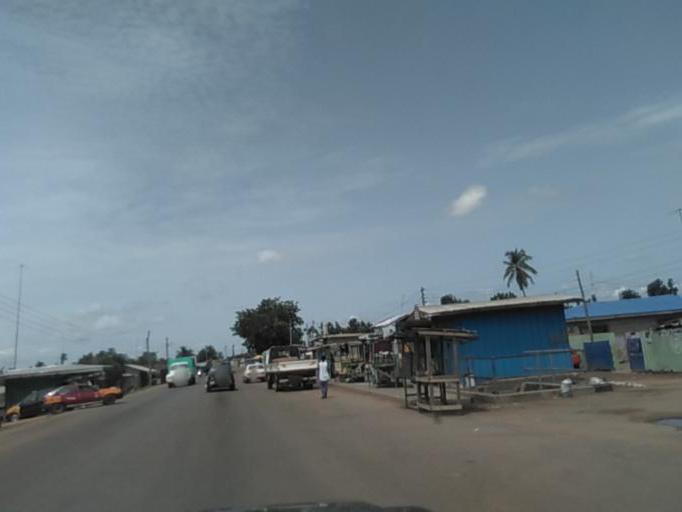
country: GH
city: Akropong
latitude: 6.1616
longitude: 0.0642
